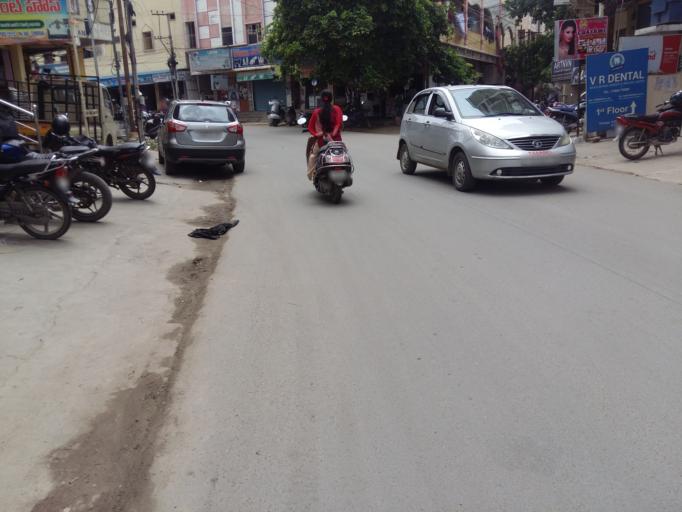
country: IN
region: Telangana
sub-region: Rangareddi
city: Kukatpalli
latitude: 17.4996
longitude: 78.4159
